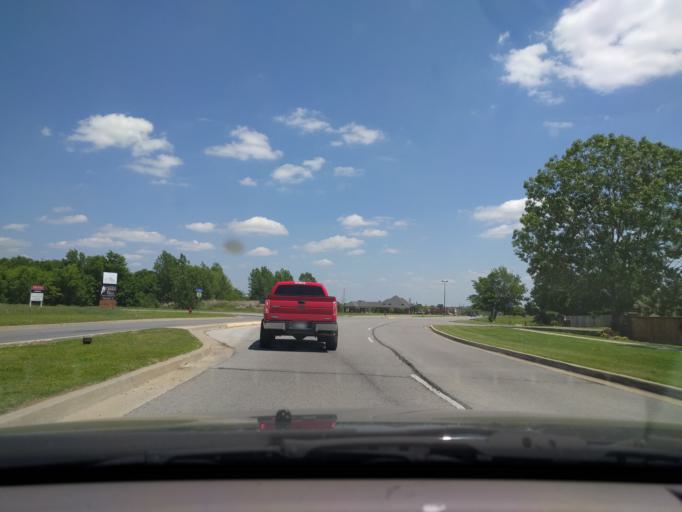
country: US
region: Oklahoma
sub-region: Tulsa County
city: Broken Arrow
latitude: 36.0752
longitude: -95.7836
